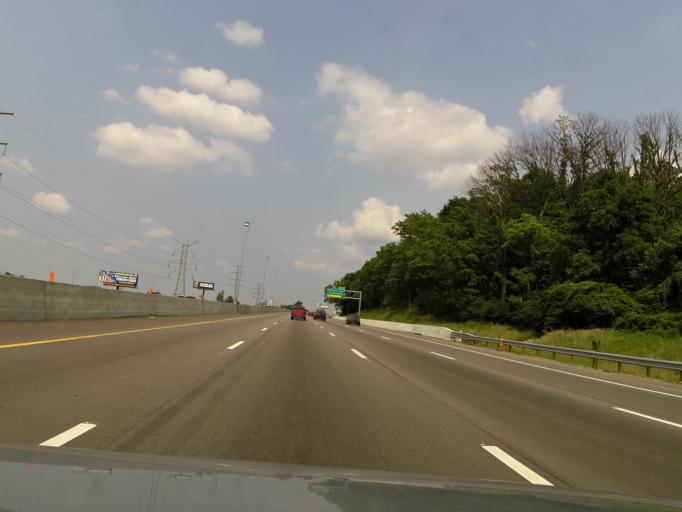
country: US
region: Ohio
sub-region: Hamilton County
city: Saint Bernard
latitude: 39.1606
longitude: -84.5237
